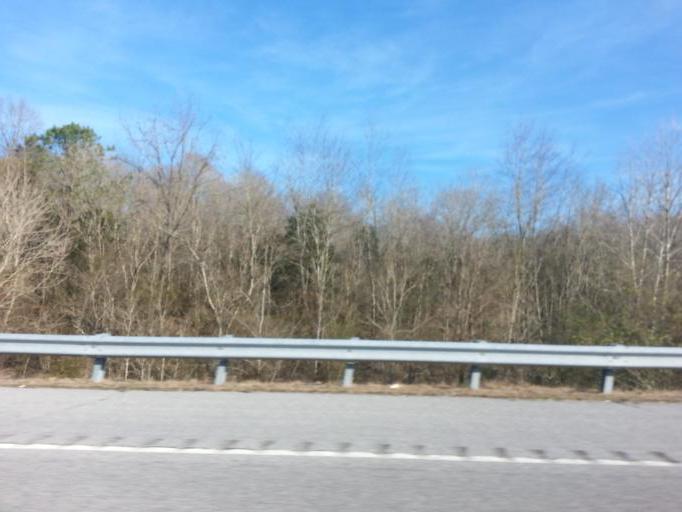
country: US
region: Tennessee
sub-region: Van Buren County
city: Spencer
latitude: 35.7810
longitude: -85.5962
